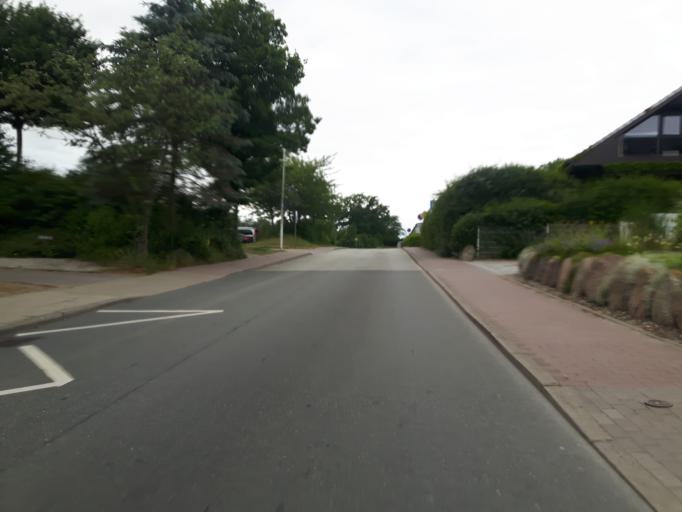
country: DE
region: Schleswig-Holstein
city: Gromitz
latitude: 54.1388
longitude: 10.9457
